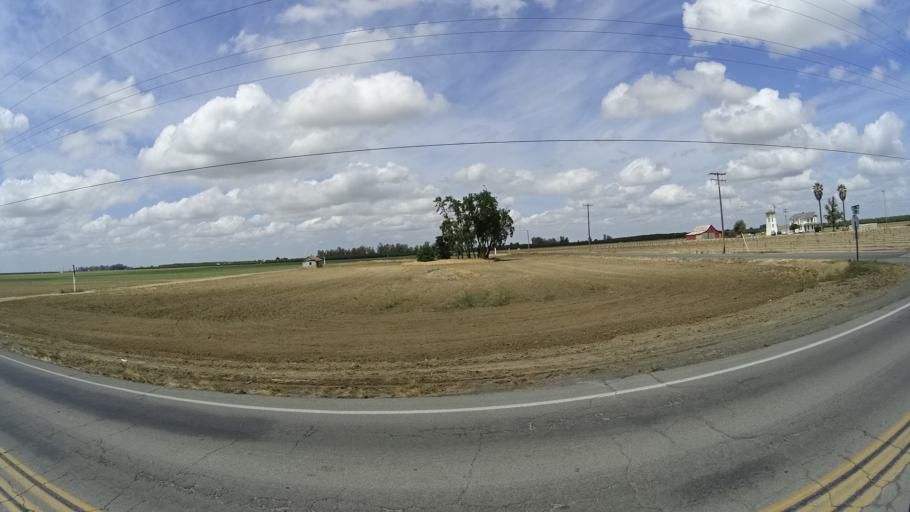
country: US
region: California
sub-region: Kings County
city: Home Garden
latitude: 36.2835
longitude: -119.6549
